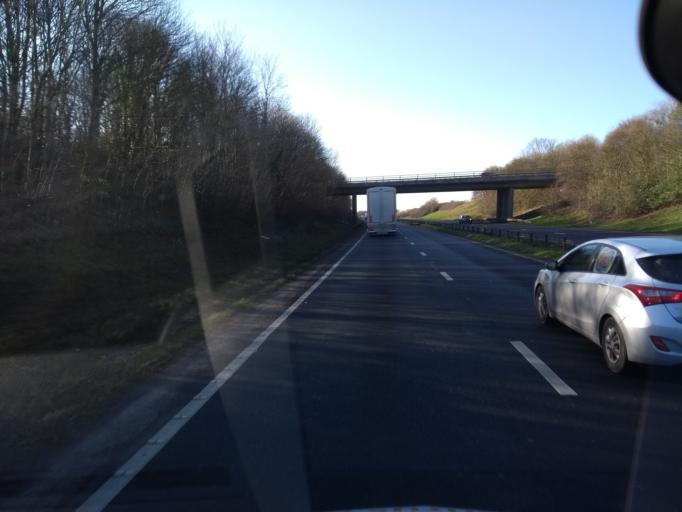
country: GB
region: England
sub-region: Somerset
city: Ilchester
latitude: 51.0146
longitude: -2.6831
